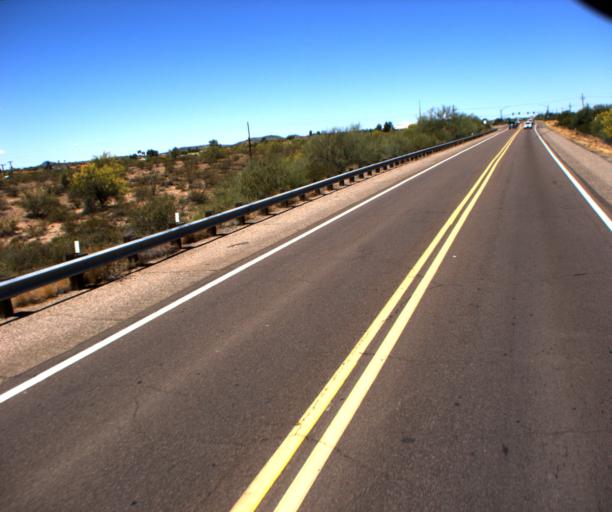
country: US
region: Arizona
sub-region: Maricopa County
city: Wickenburg
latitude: 34.0014
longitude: -112.7679
